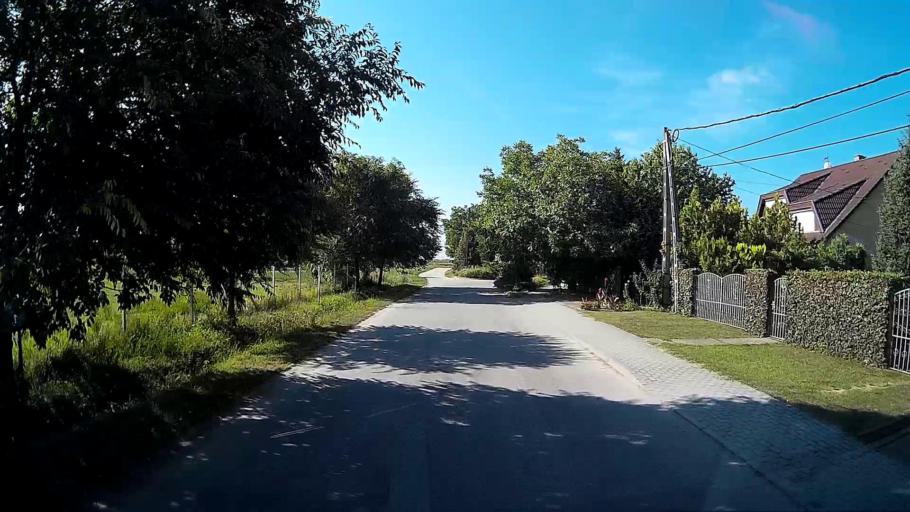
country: HU
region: Pest
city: Leanyfalu
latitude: 47.7149
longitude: 19.1003
